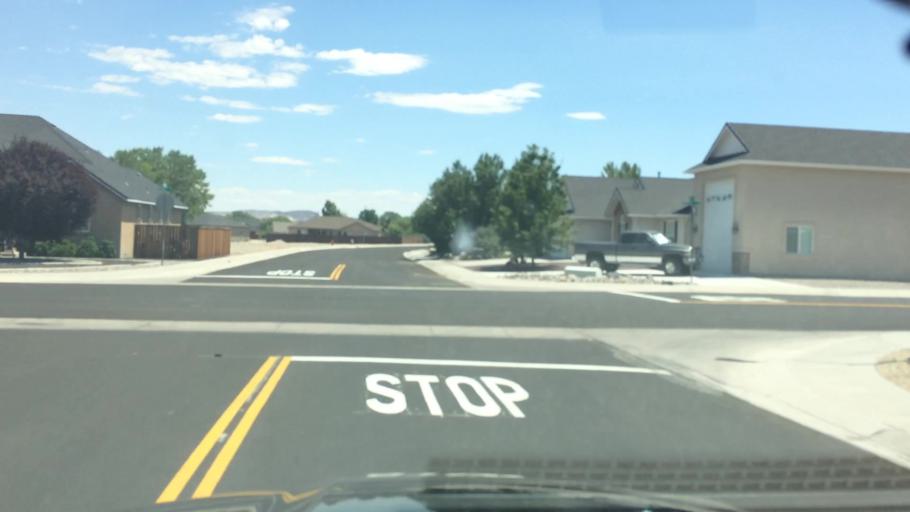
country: US
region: Nevada
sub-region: Lyon County
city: Fernley
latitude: 39.5842
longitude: -119.1446
